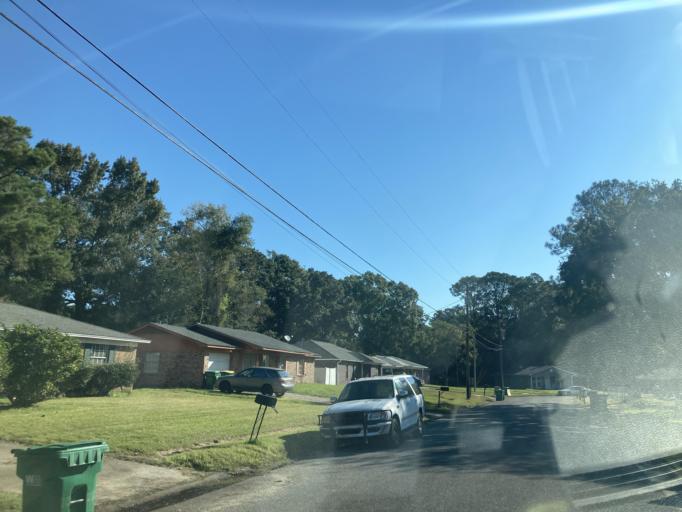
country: US
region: Mississippi
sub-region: Jackson County
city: Saint Martin
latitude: 30.4469
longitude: -88.8805
